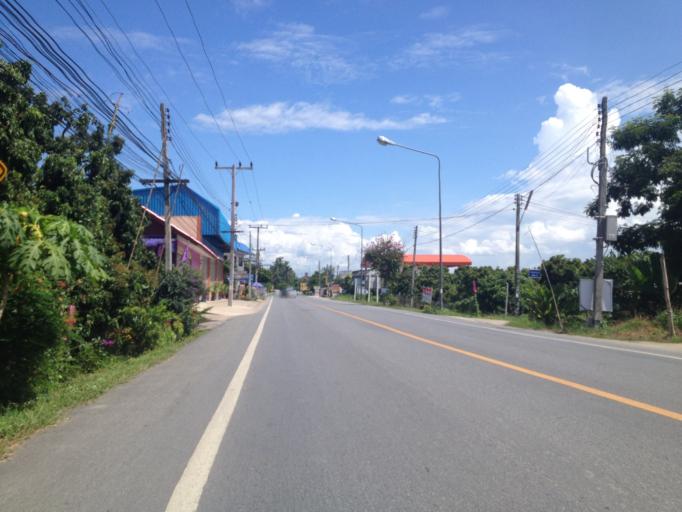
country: TH
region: Lamphun
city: Lamphun
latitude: 18.6130
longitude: 98.9580
